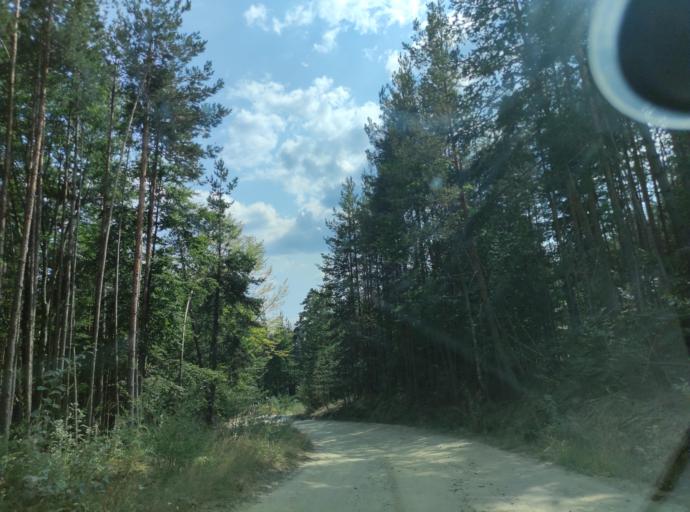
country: BG
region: Blagoevgrad
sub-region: Obshtina Belitsa
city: Belitsa
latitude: 42.0291
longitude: 23.5823
